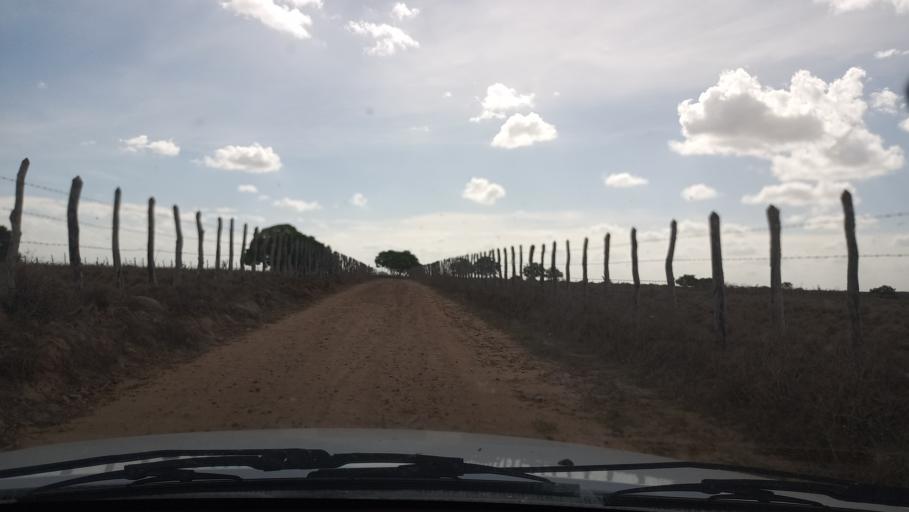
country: BR
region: Rio Grande do Norte
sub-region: Goianinha
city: Goianinha
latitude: -6.3044
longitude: -35.3030
